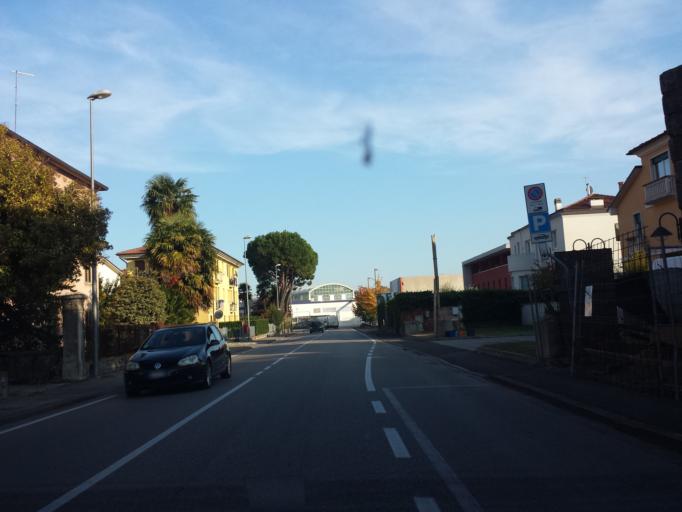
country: IT
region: Veneto
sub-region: Provincia di Vicenza
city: Schio
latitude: 45.7084
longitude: 11.3615
